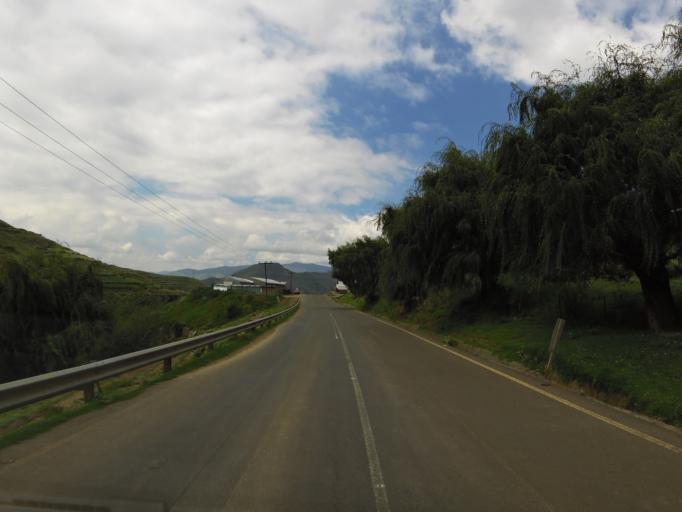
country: LS
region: Butha-Buthe
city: Butha-Buthe
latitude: -29.1093
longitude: 28.4806
